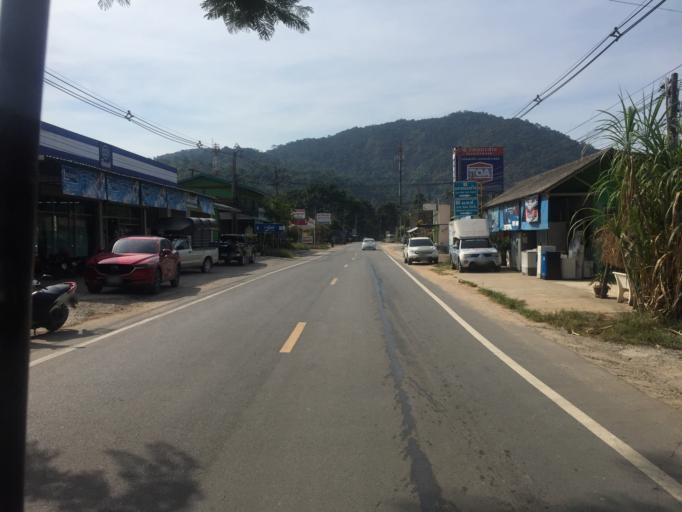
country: TH
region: Trat
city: Laem Ngop
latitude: 12.1346
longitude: 102.2760
